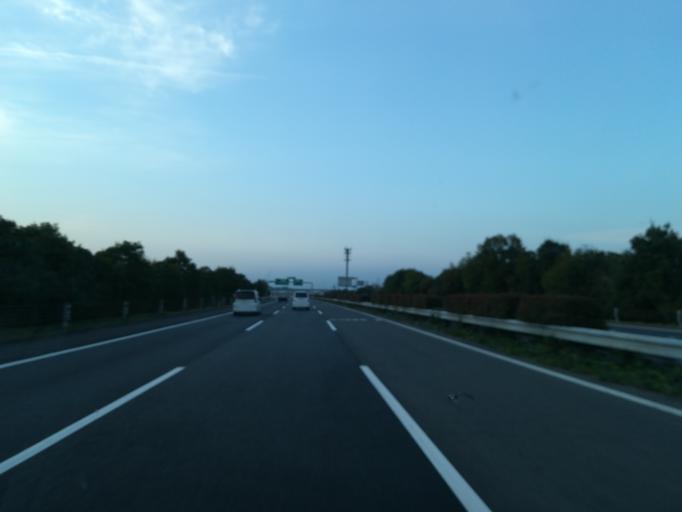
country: JP
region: Gunma
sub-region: Sawa-gun
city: Tamamura
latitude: 36.3163
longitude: 139.0825
